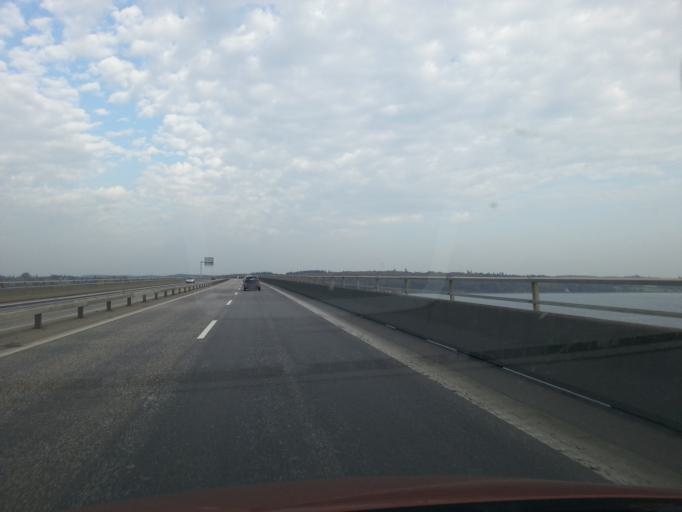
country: DK
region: Zealand
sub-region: Vordingborg Kommune
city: Nyrad
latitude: 54.9589
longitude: 11.9951
